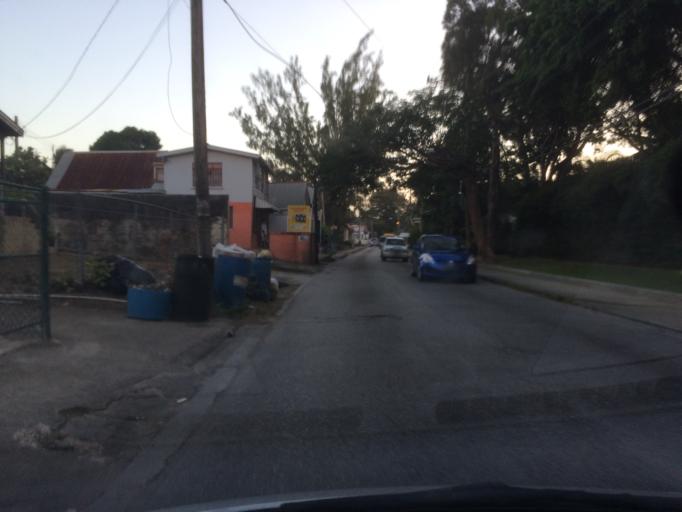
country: BB
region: Saint James
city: Holetown
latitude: 13.2103
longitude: -59.6394
